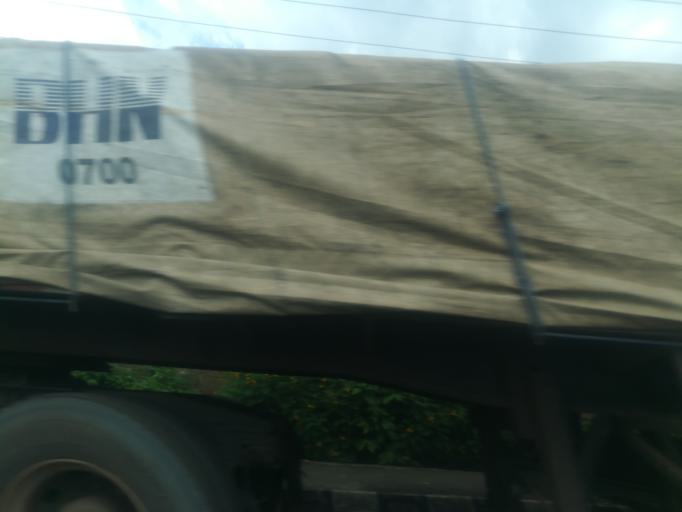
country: NG
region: Oyo
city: Ibadan
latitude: 7.4047
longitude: 3.8704
